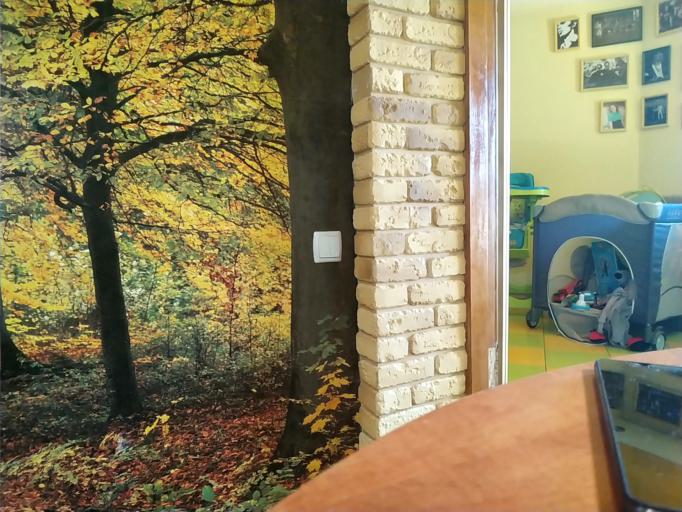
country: RU
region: Tverskaya
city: Krasnomayskiy
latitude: 57.5293
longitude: 34.1334
